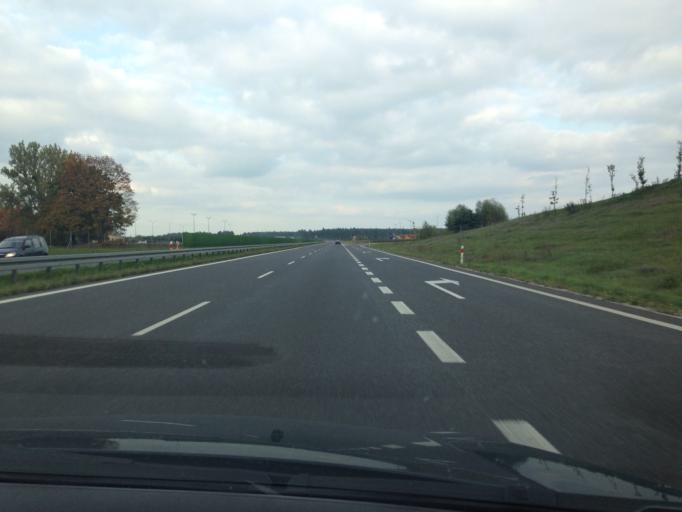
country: PL
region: Greater Poland Voivodeship
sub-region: Powiat poznanski
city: Pobiedziska
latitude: 52.4302
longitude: 17.3242
